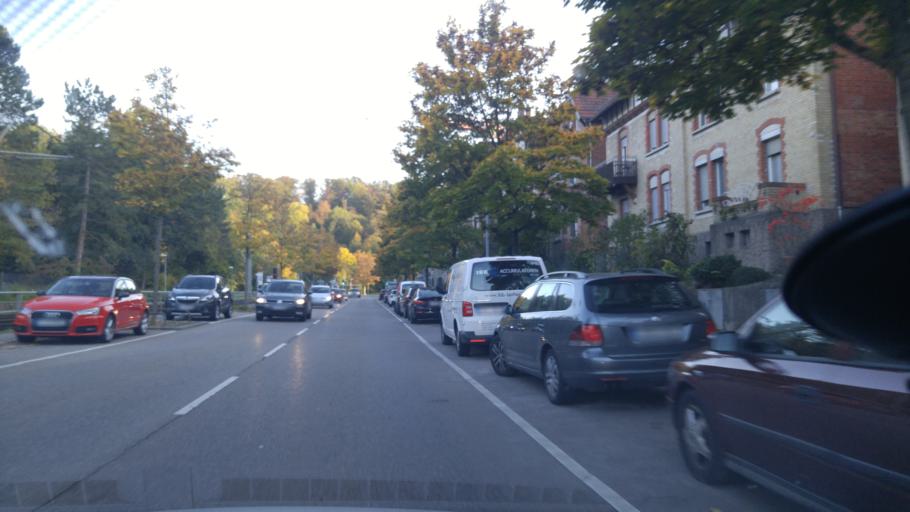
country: DE
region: Baden-Wuerttemberg
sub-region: Regierungsbezirk Stuttgart
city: Stuttgart Feuerbach
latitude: 48.7753
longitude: 9.1335
